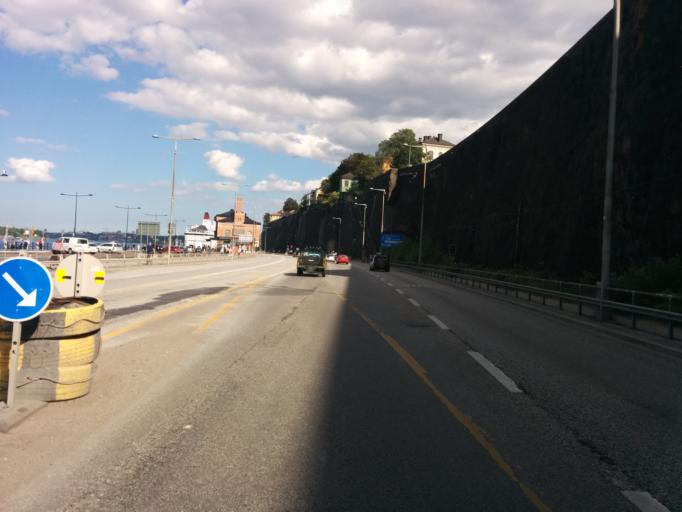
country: SE
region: Stockholm
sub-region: Stockholms Kommun
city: Stockholm
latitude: 59.3185
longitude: 18.0802
